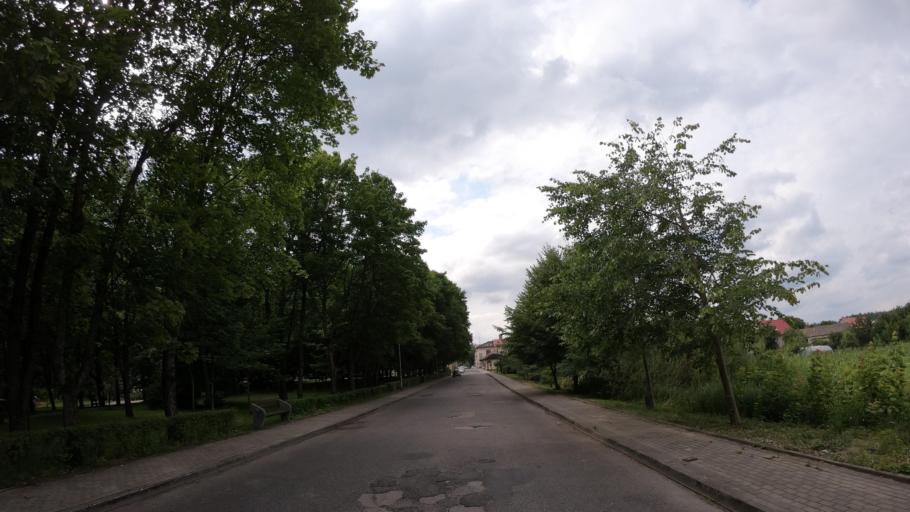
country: PL
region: West Pomeranian Voivodeship
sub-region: Powiat drawski
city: Kalisz Pomorski
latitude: 53.2963
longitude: 15.9079
